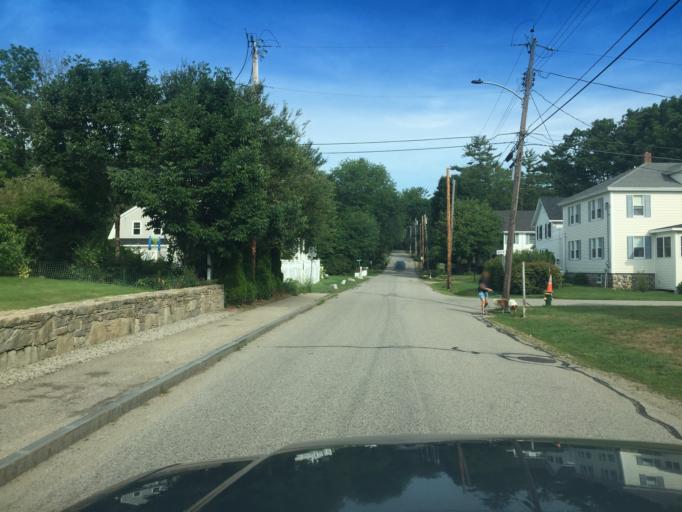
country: US
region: Maine
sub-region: York County
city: York Beach
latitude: 43.1631
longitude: -70.6220
